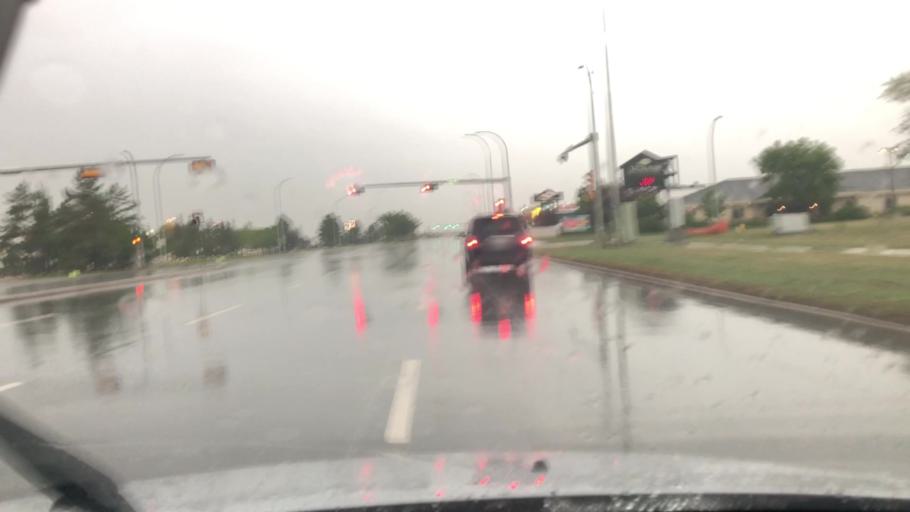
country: CA
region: Alberta
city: St. Albert
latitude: 53.5945
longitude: -113.5698
